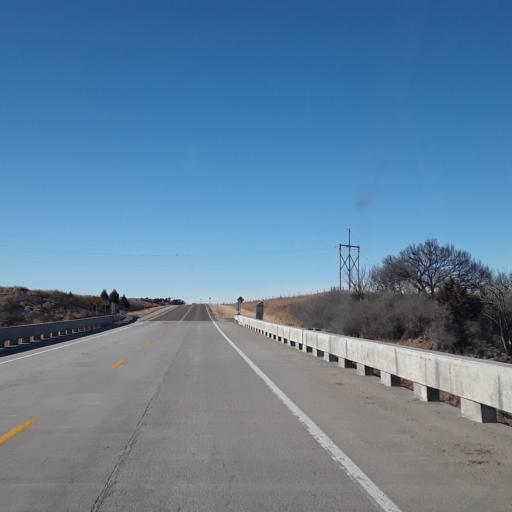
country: US
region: Nebraska
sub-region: Frontier County
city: Stockville
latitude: 40.6318
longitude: -100.5667
